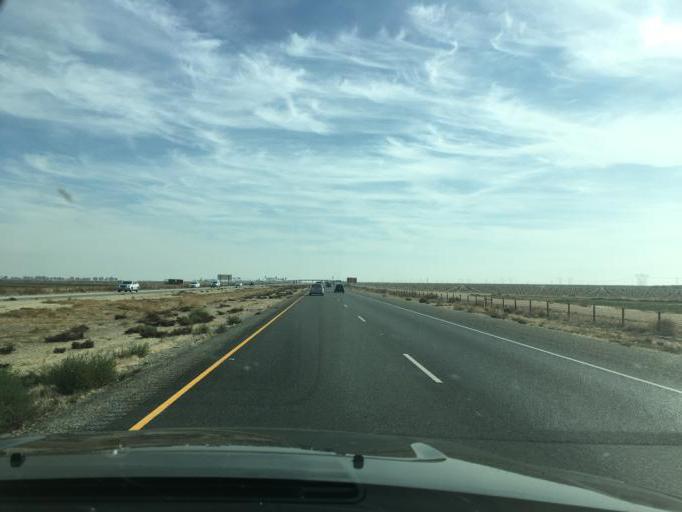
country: US
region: California
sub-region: Kern County
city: Buttonwillow
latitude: 35.3635
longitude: -119.3483
